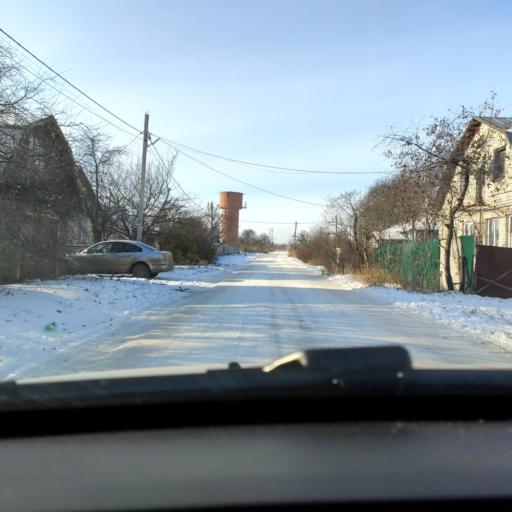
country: RU
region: Voronezj
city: Devitsa
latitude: 51.6025
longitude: 38.9914
